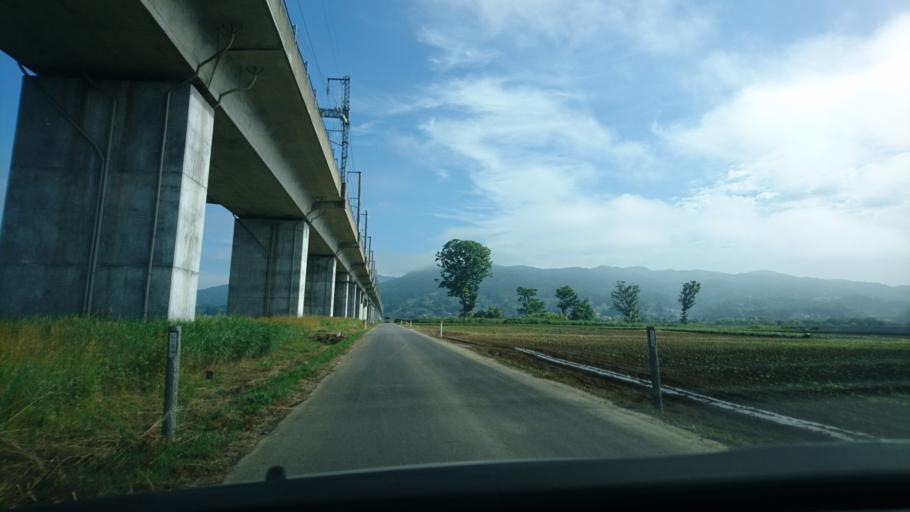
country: JP
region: Iwate
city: Ichinoseki
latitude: 38.9610
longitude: 141.1518
